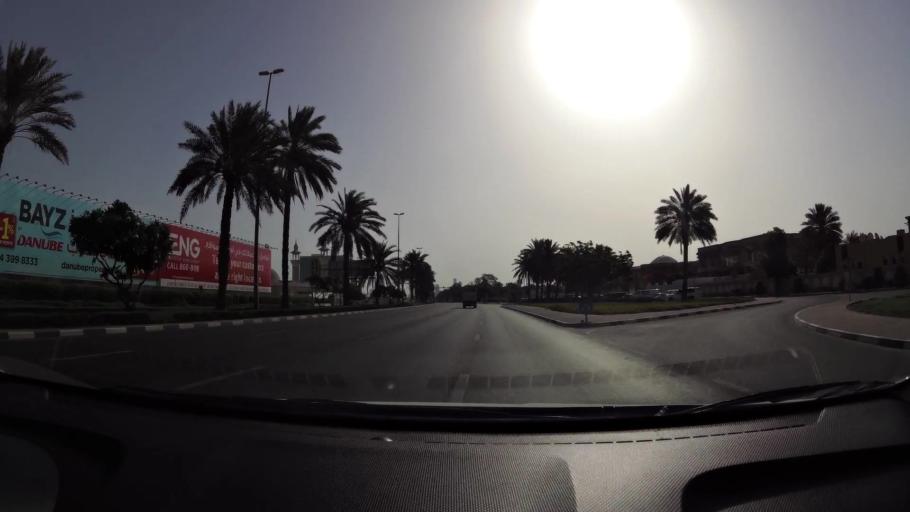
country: AE
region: Ash Shariqah
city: Sharjah
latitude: 25.2931
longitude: 55.3288
